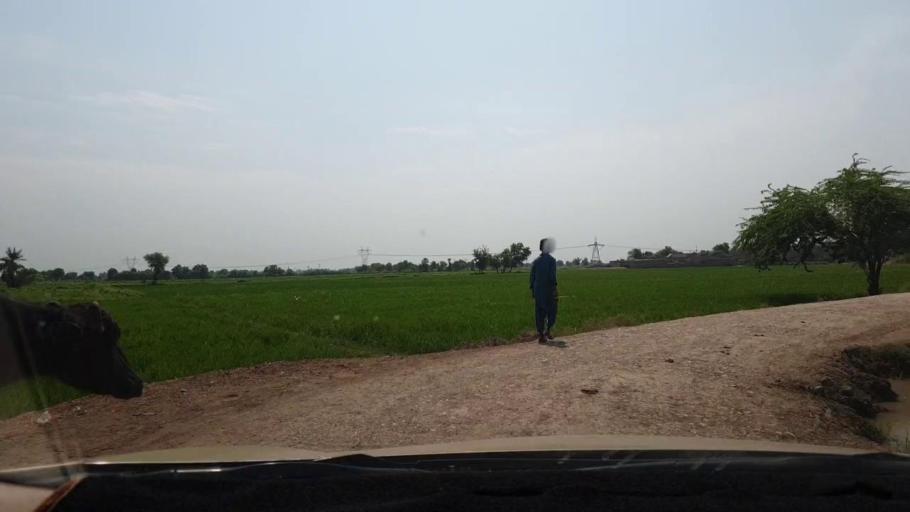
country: PK
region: Sindh
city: Naudero
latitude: 27.6498
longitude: 68.2603
